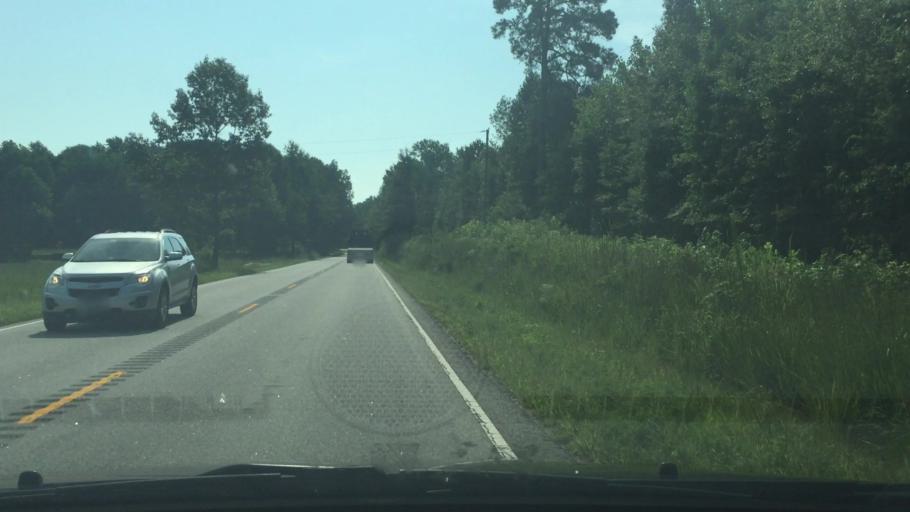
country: US
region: Virginia
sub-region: Sussex County
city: Sussex
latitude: 36.9751
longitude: -77.2070
